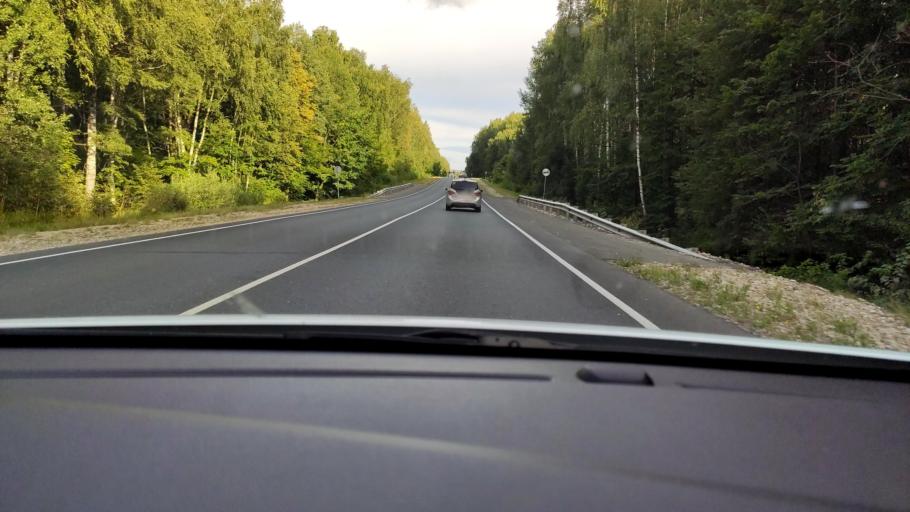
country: RU
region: Mariy-El
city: Krasnogorskiy
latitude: 56.1876
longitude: 48.2472
